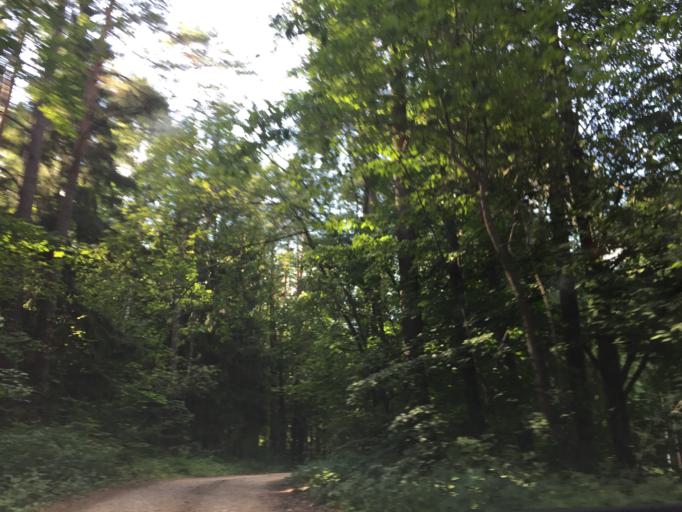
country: LV
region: Krimulda
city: Ragana
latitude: 57.1363
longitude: 24.7689
